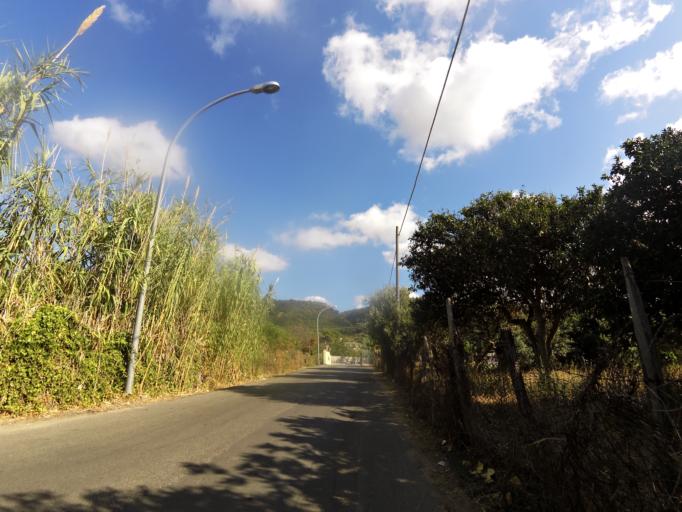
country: IT
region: Calabria
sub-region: Provincia di Vibo-Valentia
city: Santa Domenica
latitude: 38.6679
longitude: 15.8728
